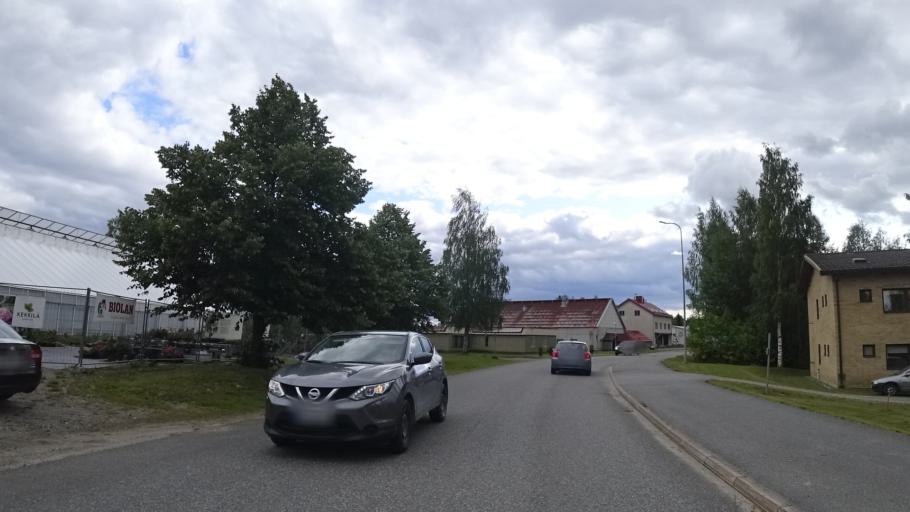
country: FI
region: North Karelia
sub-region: Joensuu
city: Ilomantsi
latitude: 62.6701
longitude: 30.9379
